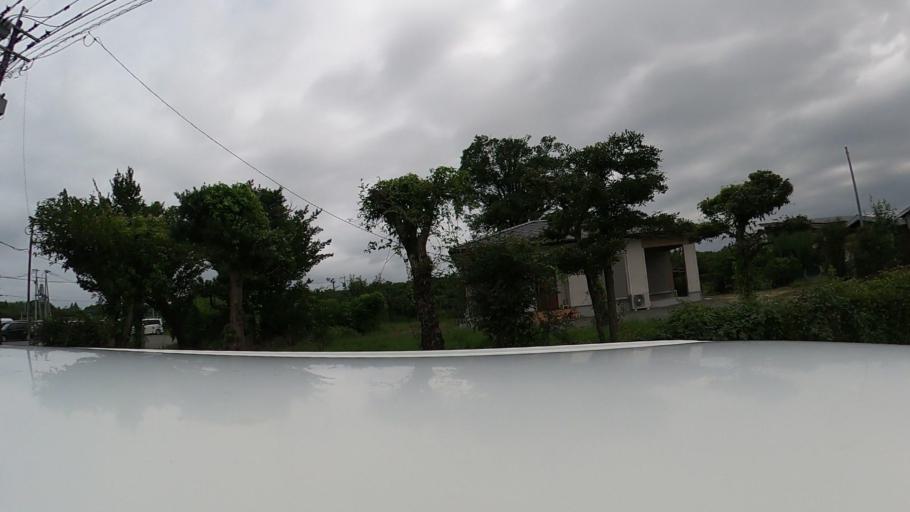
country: JP
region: Kumamoto
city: Ozu
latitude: 32.8366
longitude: 130.8773
